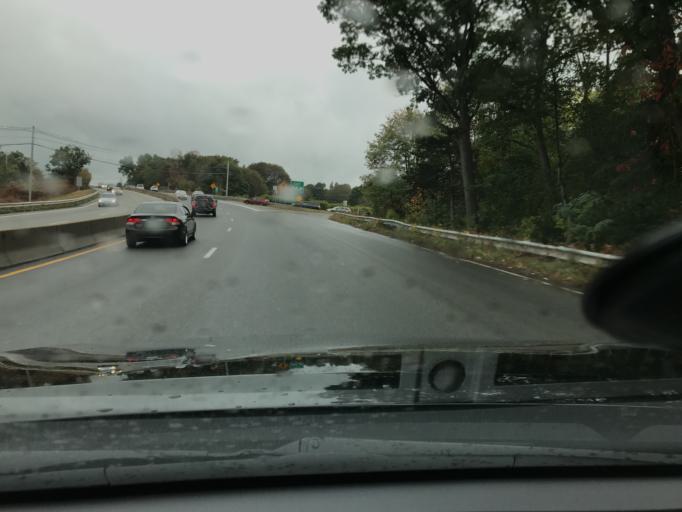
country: US
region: Massachusetts
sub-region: Essex County
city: Peabody
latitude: 42.5350
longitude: -70.9494
